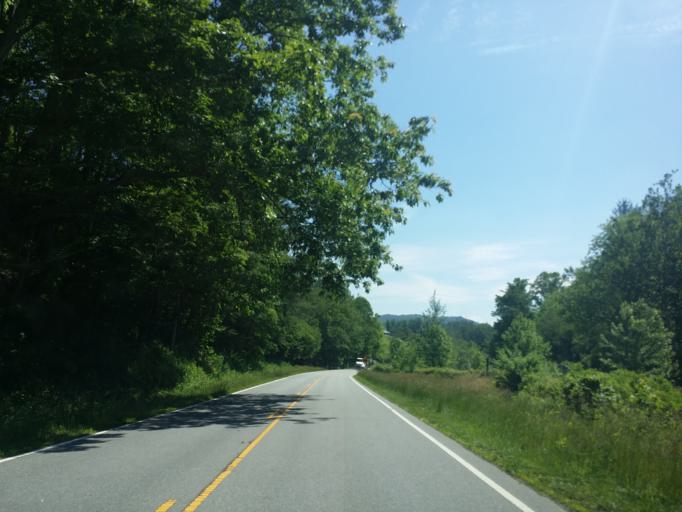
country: US
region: North Carolina
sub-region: Madison County
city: Marshall
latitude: 35.7028
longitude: -82.8000
